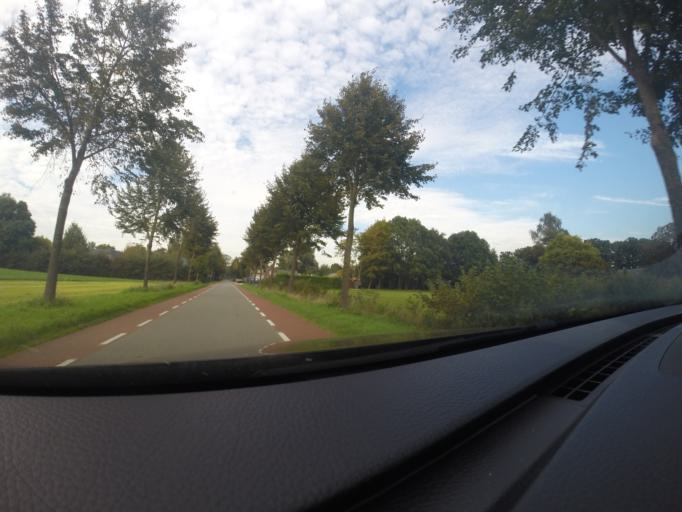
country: NL
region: Gelderland
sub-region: Gemeente Bronckhorst
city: Hengelo
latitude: 52.0193
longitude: 6.2946
